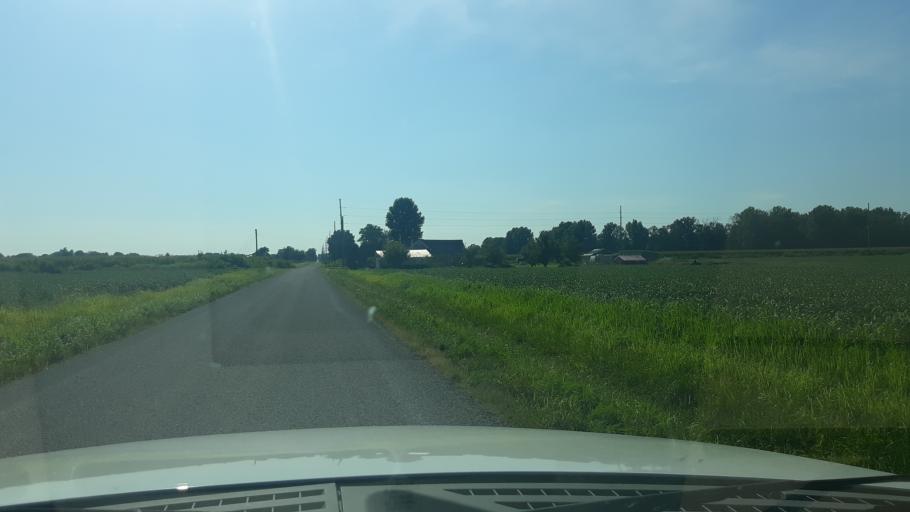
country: US
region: Illinois
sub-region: Saline County
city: Eldorado
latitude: 37.8630
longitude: -88.5021
